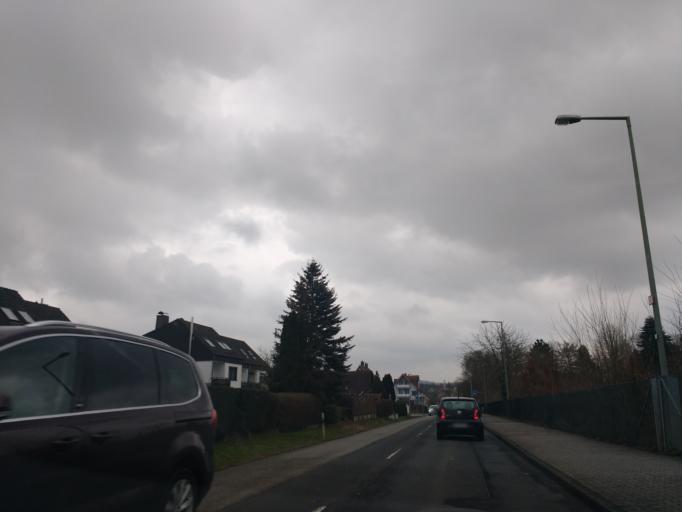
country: DE
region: Hesse
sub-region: Regierungsbezirk Kassel
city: Fuldabruck
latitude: 51.2831
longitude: 9.4532
